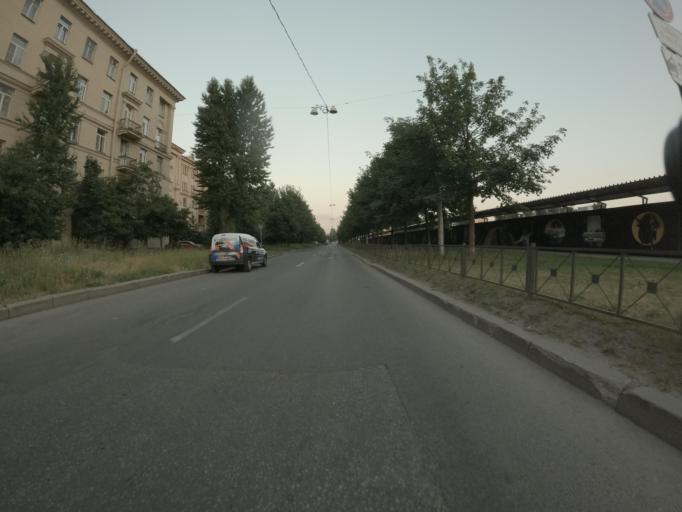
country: RU
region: St.-Petersburg
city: Centralniy
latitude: 59.9303
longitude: 30.4052
